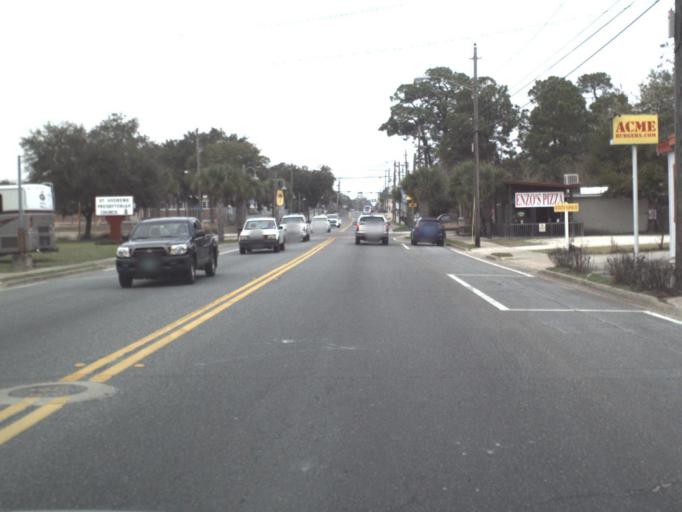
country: US
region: Florida
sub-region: Bay County
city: Pretty Bayou
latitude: 30.1728
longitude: -85.7015
